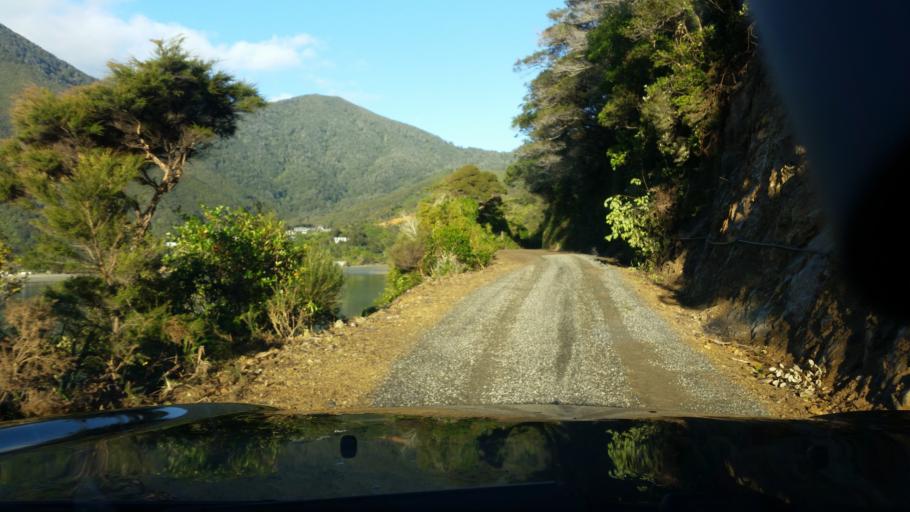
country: NZ
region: Marlborough
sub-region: Marlborough District
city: Picton
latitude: -41.1037
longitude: 173.6579
